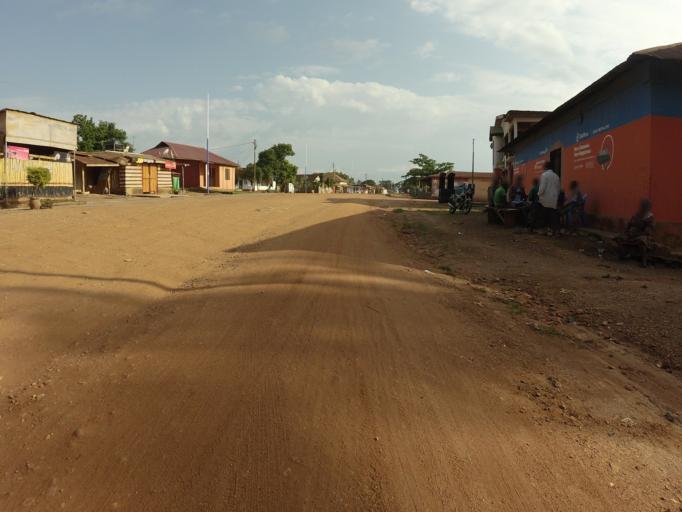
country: GH
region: Volta
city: Hohoe
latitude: 7.1242
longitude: 0.4598
